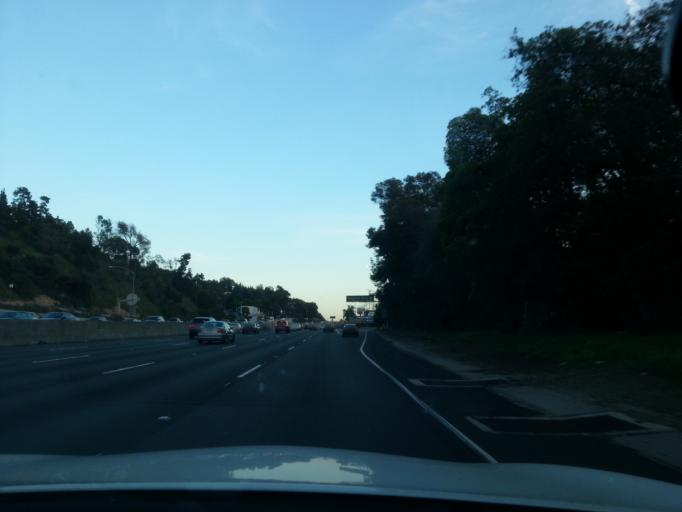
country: US
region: California
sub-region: Los Angeles County
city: Universal City
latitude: 34.1312
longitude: -118.3497
